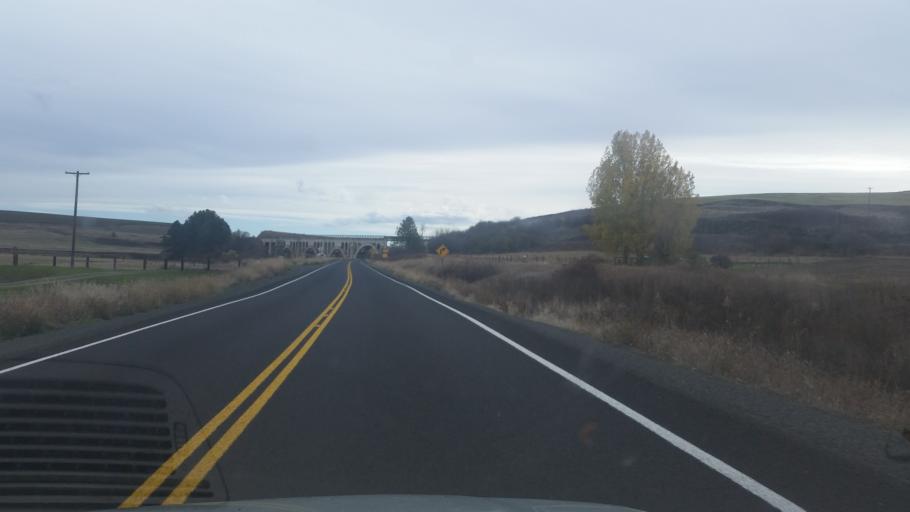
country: US
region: Washington
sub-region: Spokane County
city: Cheney
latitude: 47.2243
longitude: -117.3669
